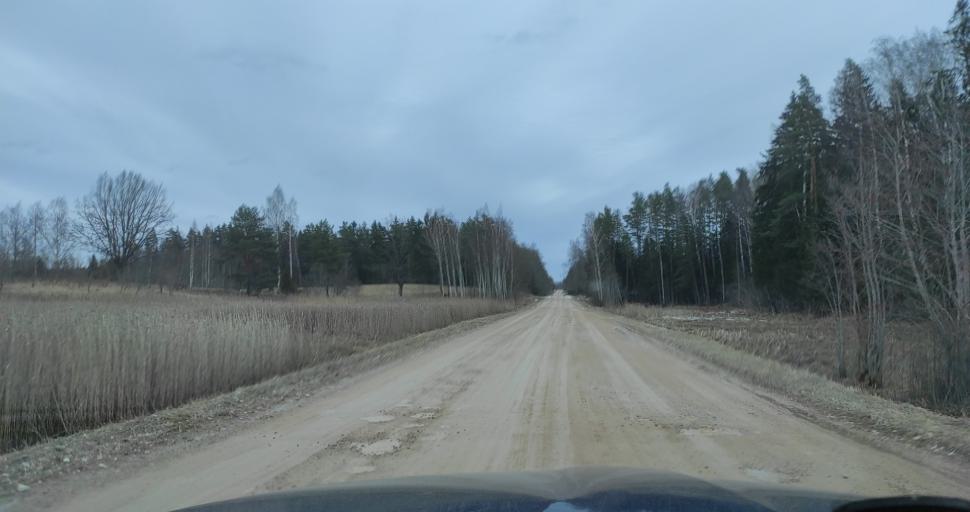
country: LV
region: Tukuma Rajons
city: Tukums
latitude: 57.0801
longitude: 23.0714
